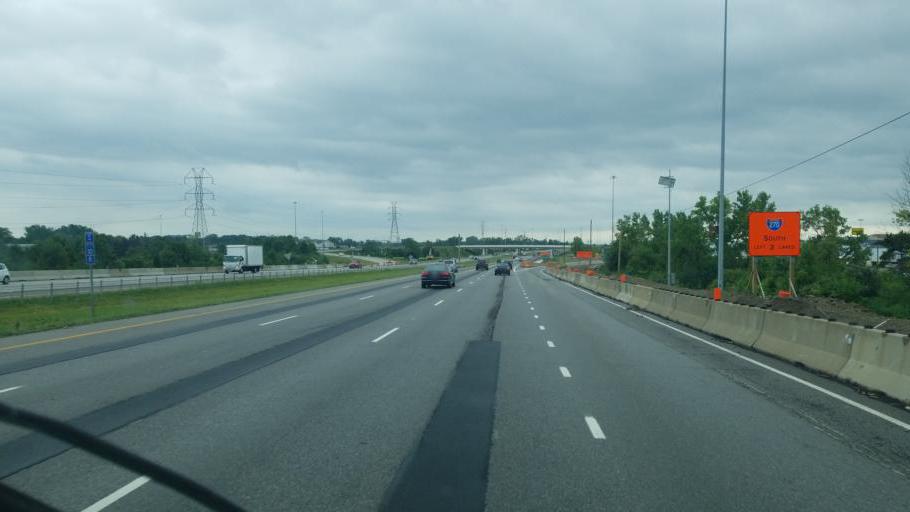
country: US
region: Ohio
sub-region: Franklin County
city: Hilliard
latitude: 40.0072
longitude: -83.1190
